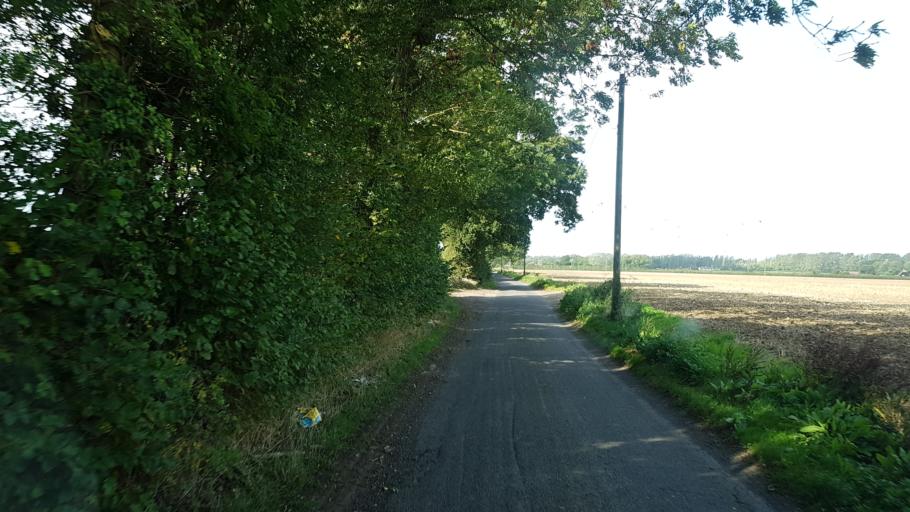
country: GB
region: England
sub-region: Kent
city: Harrietsham
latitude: 51.2380
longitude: 0.6098
